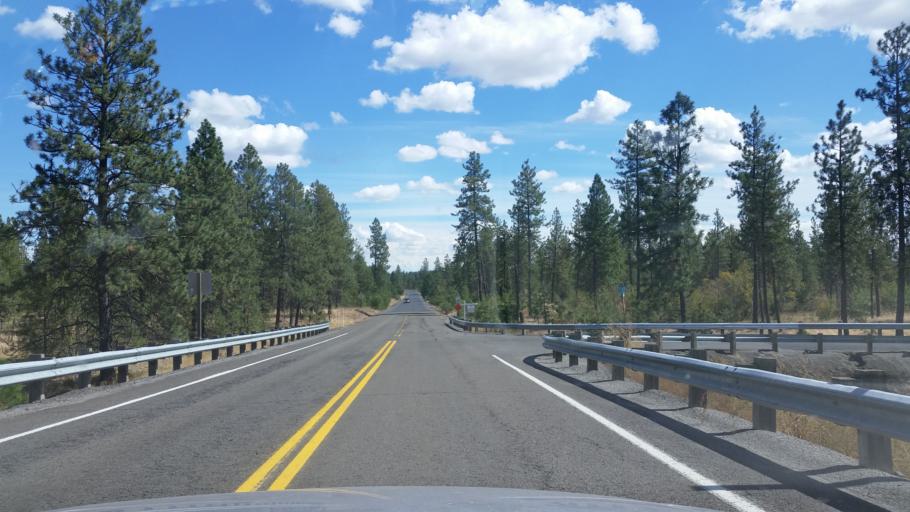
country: US
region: Washington
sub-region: Spokane County
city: Medical Lake
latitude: 47.5039
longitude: -117.6888
